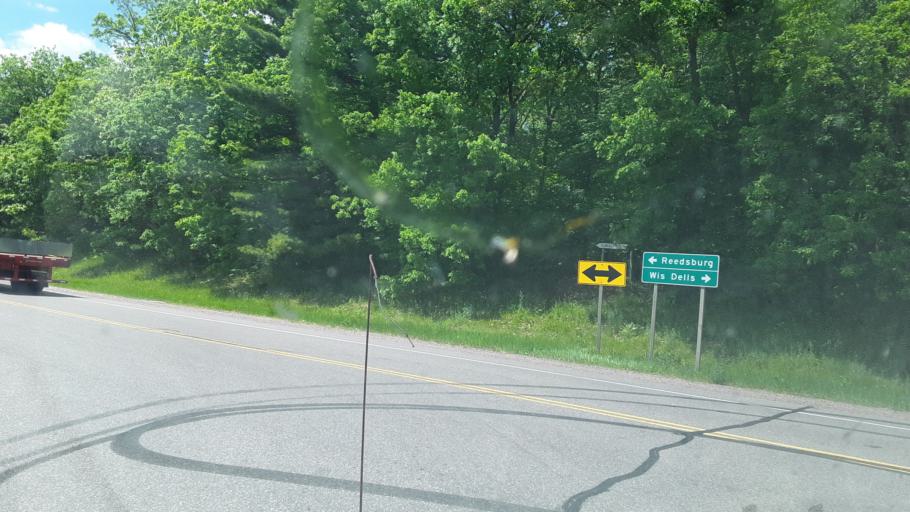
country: US
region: Wisconsin
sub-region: Sauk County
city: Reedsburg
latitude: 43.5926
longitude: -89.9102
